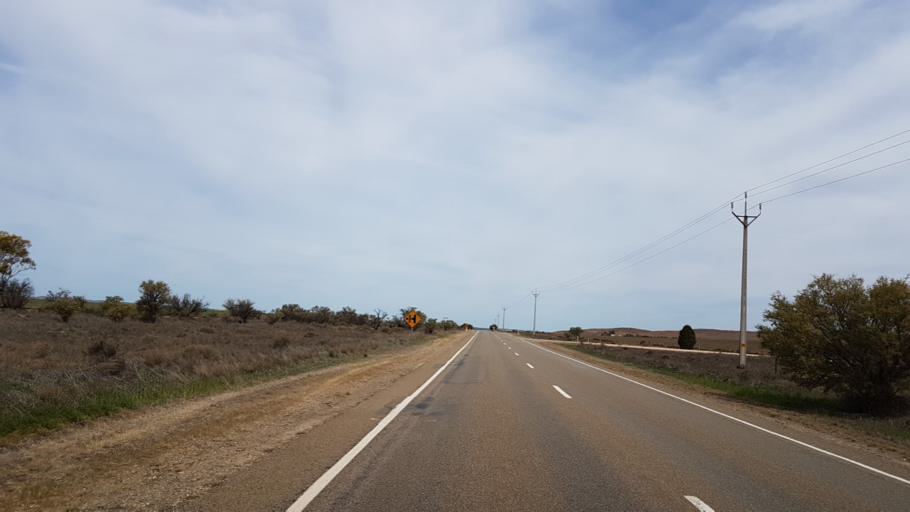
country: AU
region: South Australia
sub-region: Peterborough
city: Peterborough
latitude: -33.0140
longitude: 138.7608
